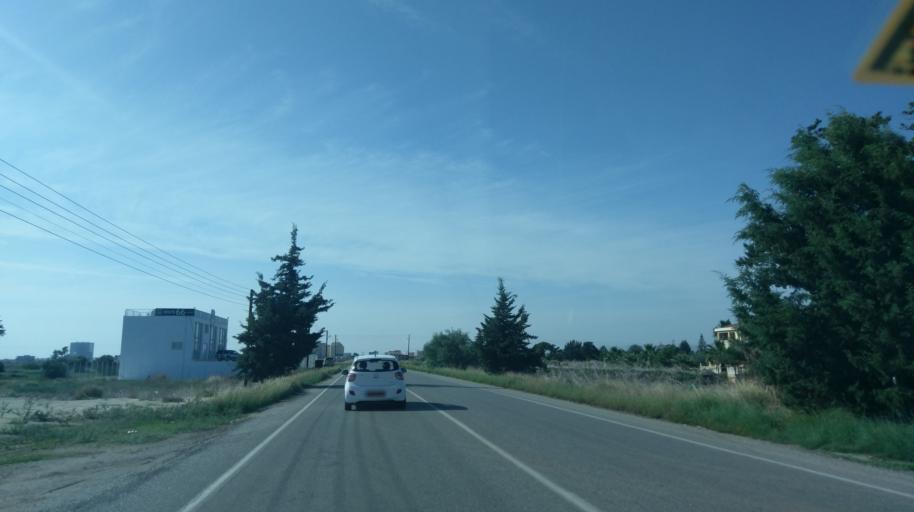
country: CY
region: Ammochostos
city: Trikomo
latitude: 35.2794
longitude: 33.9128
